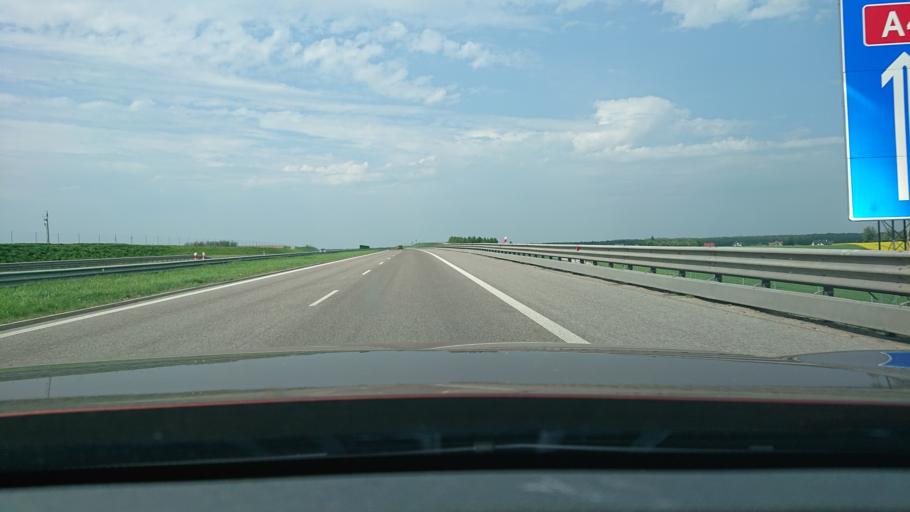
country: PL
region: Subcarpathian Voivodeship
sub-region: Powiat jaroslawski
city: Pawlosiow
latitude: 49.9570
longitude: 22.6606
